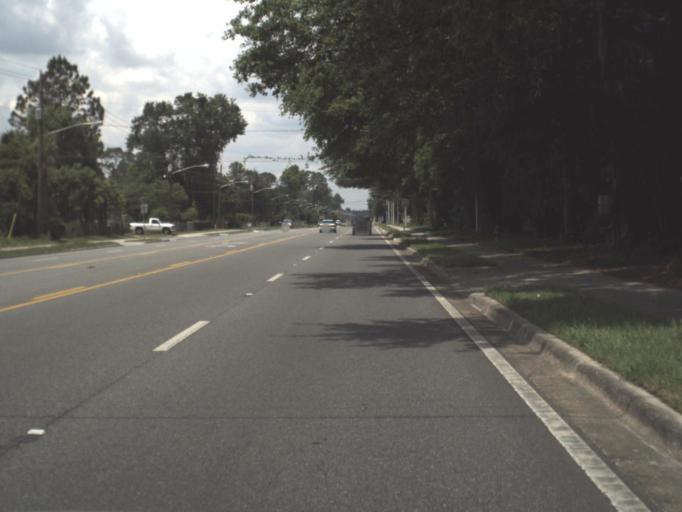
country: US
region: Florida
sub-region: Columbia County
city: Five Points
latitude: 30.2250
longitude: -82.6384
